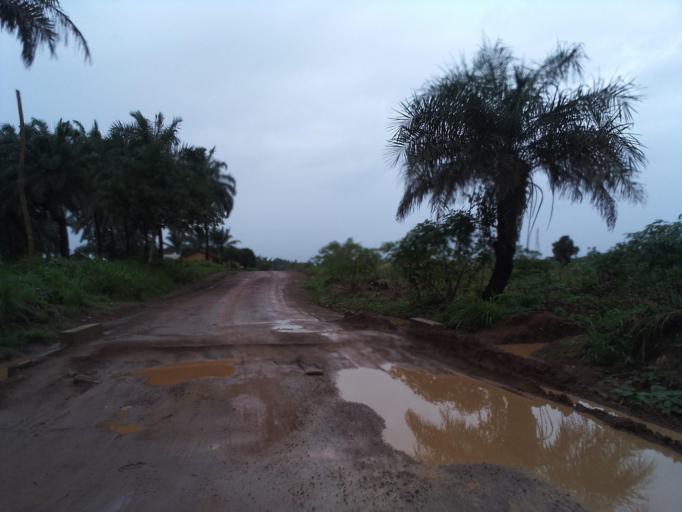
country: SL
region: Eastern Province
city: Kenema
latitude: 7.8761
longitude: -11.1539
